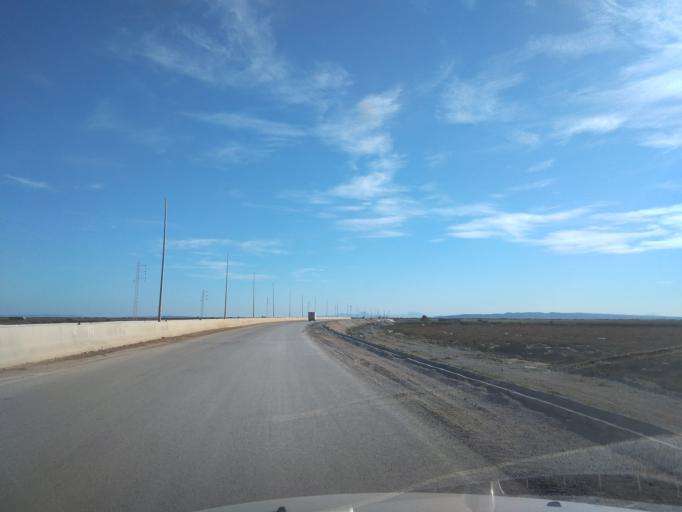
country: TN
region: Ariana
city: Qal'at al Andalus
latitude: 37.0403
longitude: 10.1313
